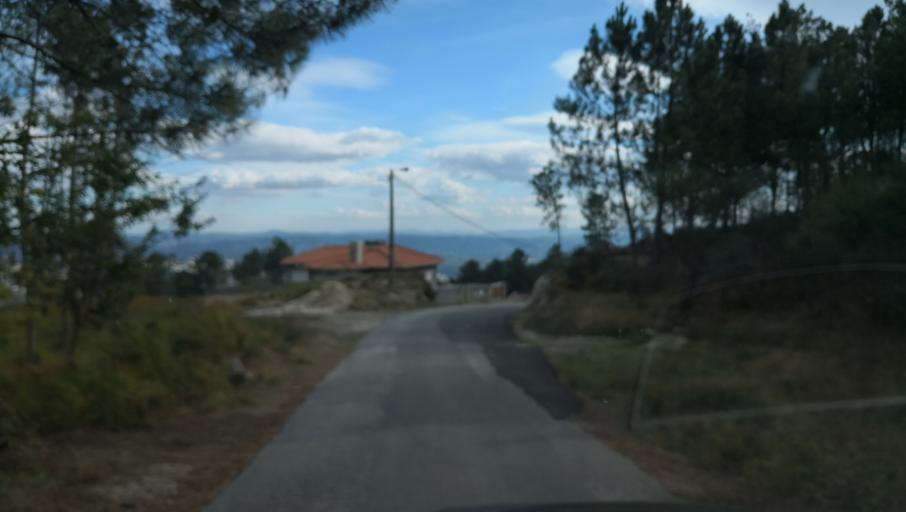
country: PT
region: Vila Real
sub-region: Vila Real
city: Vila Real
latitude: 41.3241
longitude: -7.7757
